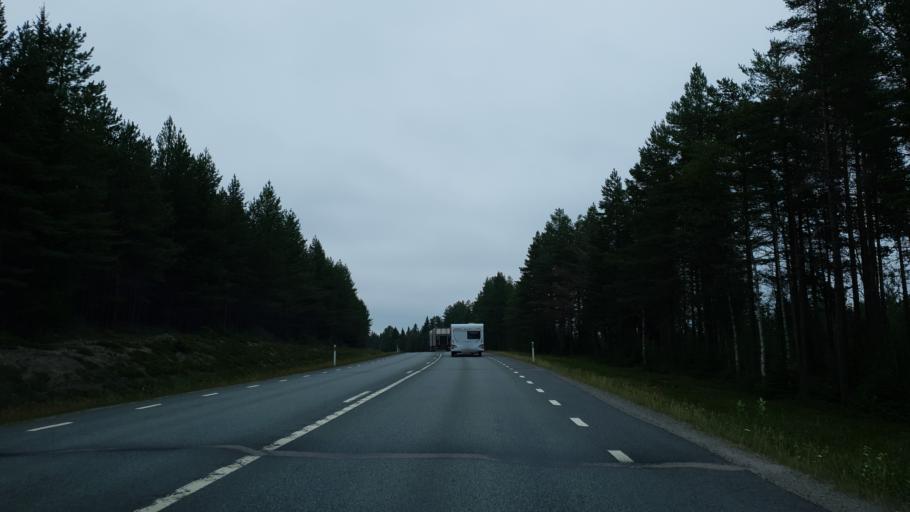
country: SE
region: Vaesterbotten
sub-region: Skelleftea Kommun
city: Burea
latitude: 64.3474
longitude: 21.2896
